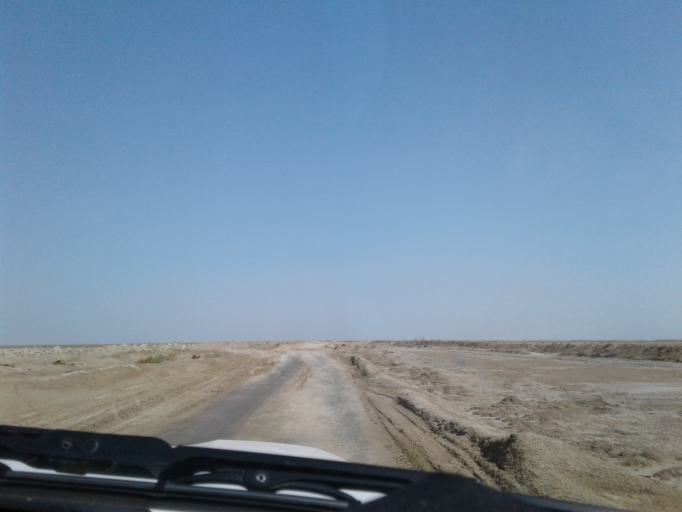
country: IR
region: Golestan
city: Gomishan
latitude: 37.8301
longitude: 53.9215
